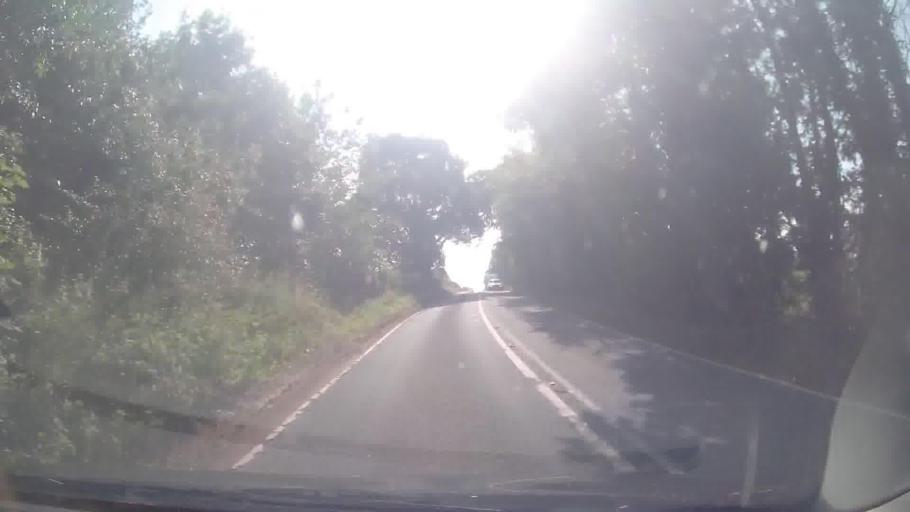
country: GB
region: England
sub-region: Cheshire West and Chester
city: Tiverton
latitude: 53.1156
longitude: -2.6609
